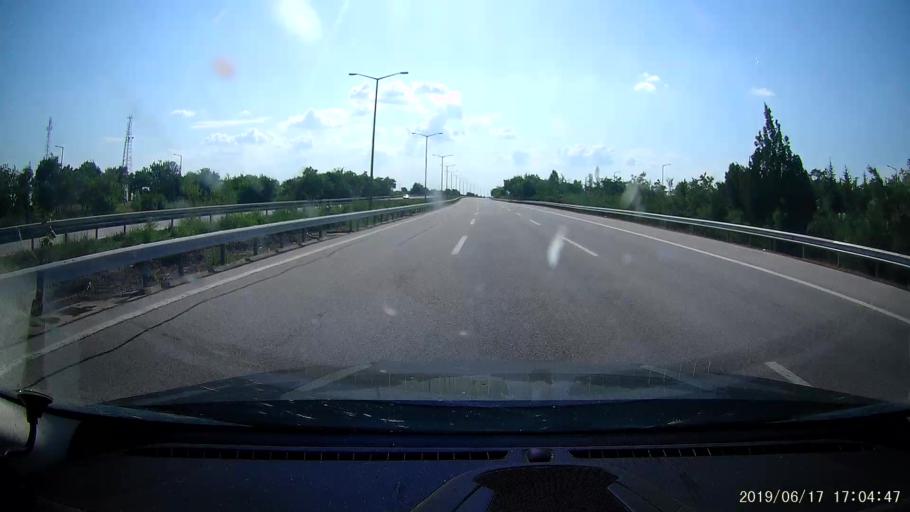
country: TR
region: Edirne
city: Haskoy
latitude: 41.6571
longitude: 26.7170
